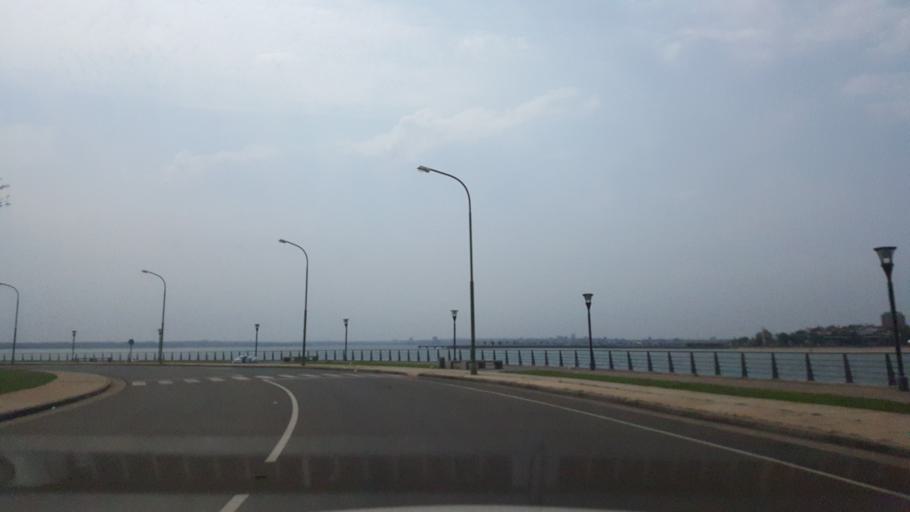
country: AR
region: Misiones
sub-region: Departamento de Capital
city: Posadas
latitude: -27.3557
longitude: -55.9105
